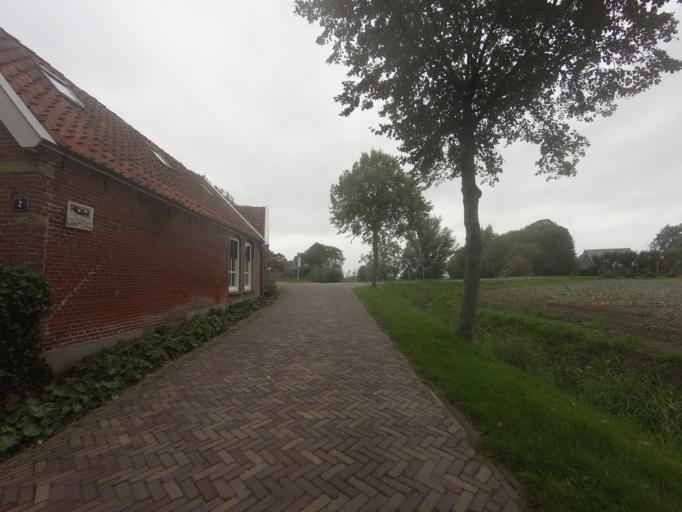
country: NL
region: Friesland
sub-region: Gemeente Ferwerderadiel
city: Ferwert
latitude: 53.3364
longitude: 5.8525
